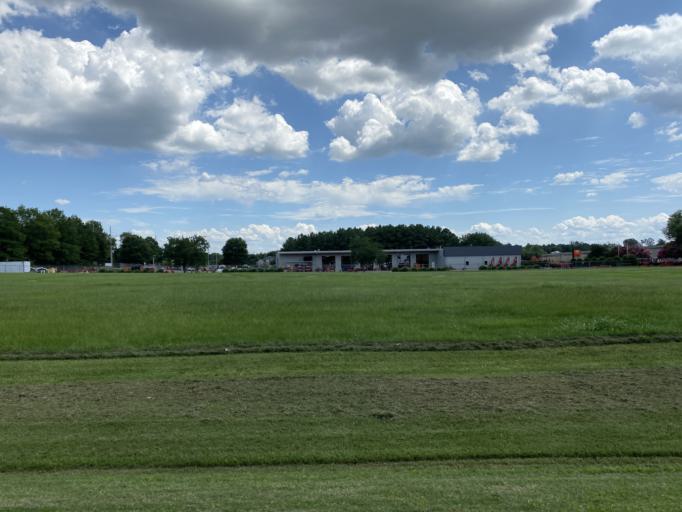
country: US
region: Alabama
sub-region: Madison County
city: Redstone Arsenal
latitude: 34.7572
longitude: -86.6710
